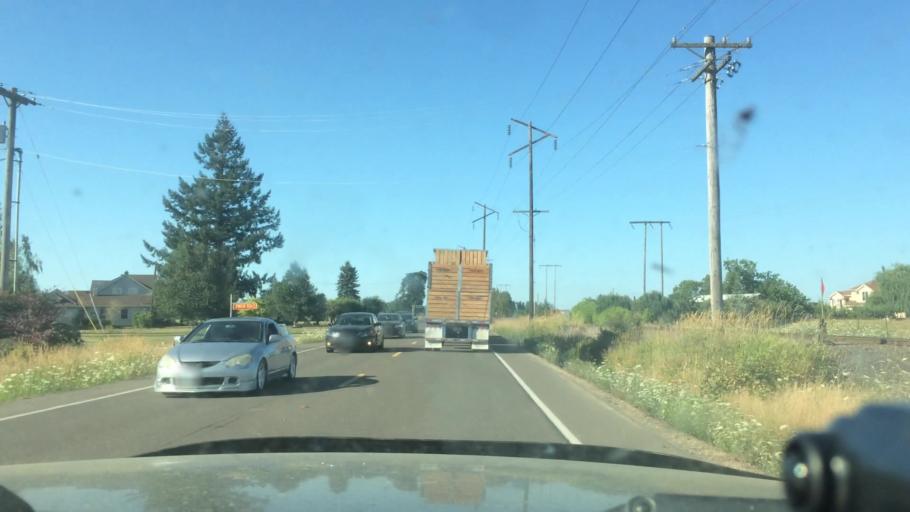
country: US
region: Oregon
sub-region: Marion County
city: Hayesville
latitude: 45.0523
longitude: -122.9864
